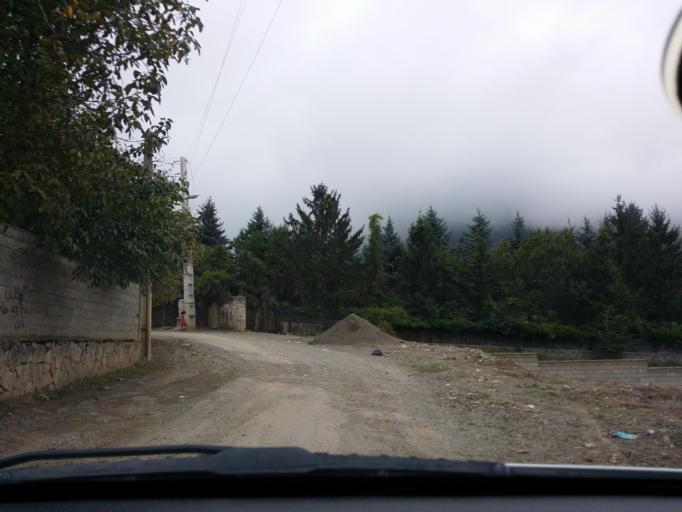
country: IR
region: Mazandaran
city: `Abbasabad
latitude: 36.4905
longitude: 51.1433
